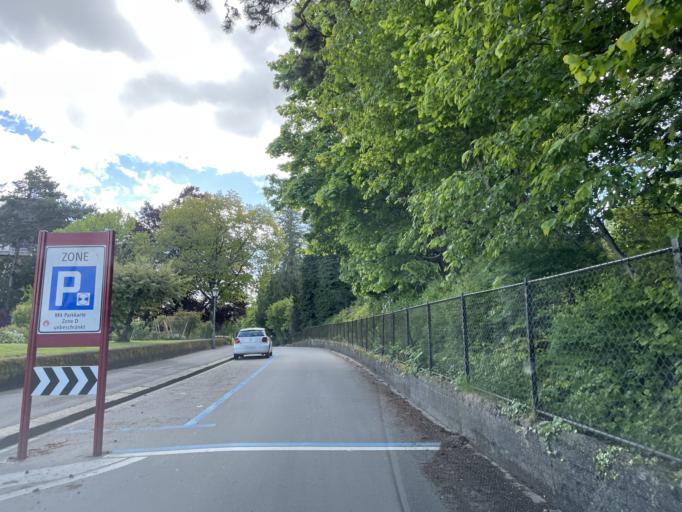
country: CH
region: Zurich
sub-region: Bezirk Winterthur
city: Stadt Winterthur (Kreis 1) / Heiligberg
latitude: 47.4959
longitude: 8.7237
